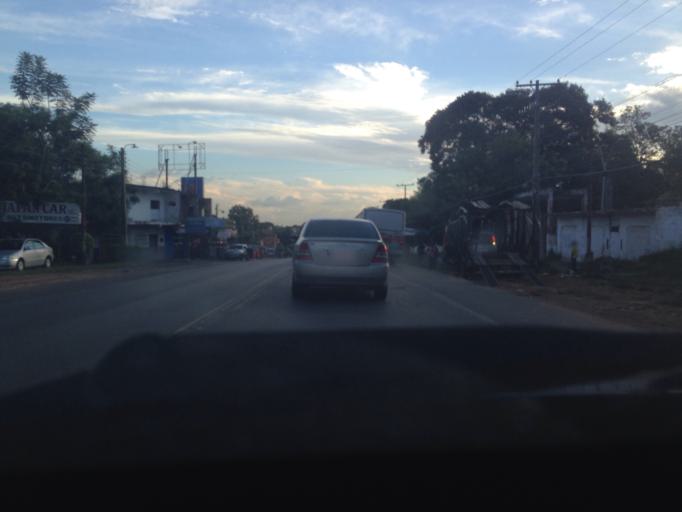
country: PY
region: Central
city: Lambare
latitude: -25.3494
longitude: -57.5908
